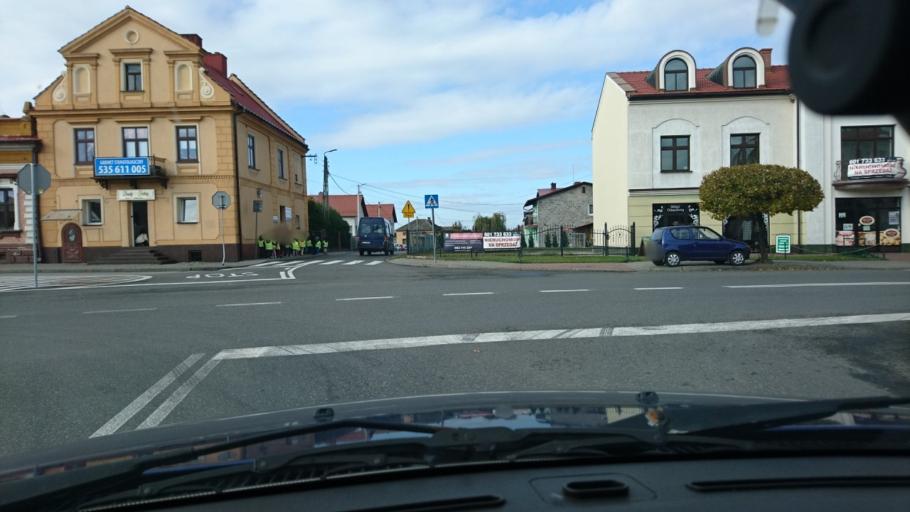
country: PL
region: Silesian Voivodeship
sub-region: Powiat bielski
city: Wilamowice
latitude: 49.9166
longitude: 19.1523
